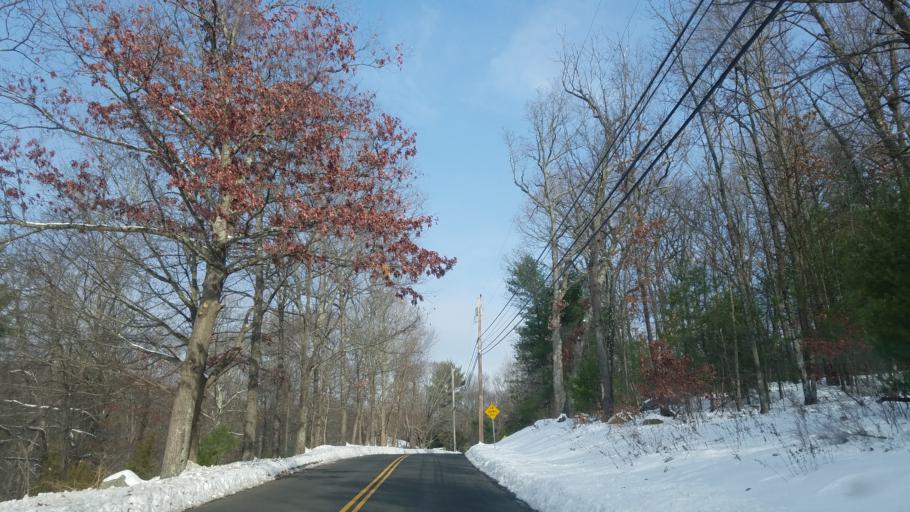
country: US
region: Connecticut
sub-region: Hartford County
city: Canton Valley
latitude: 41.8374
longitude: -72.9048
